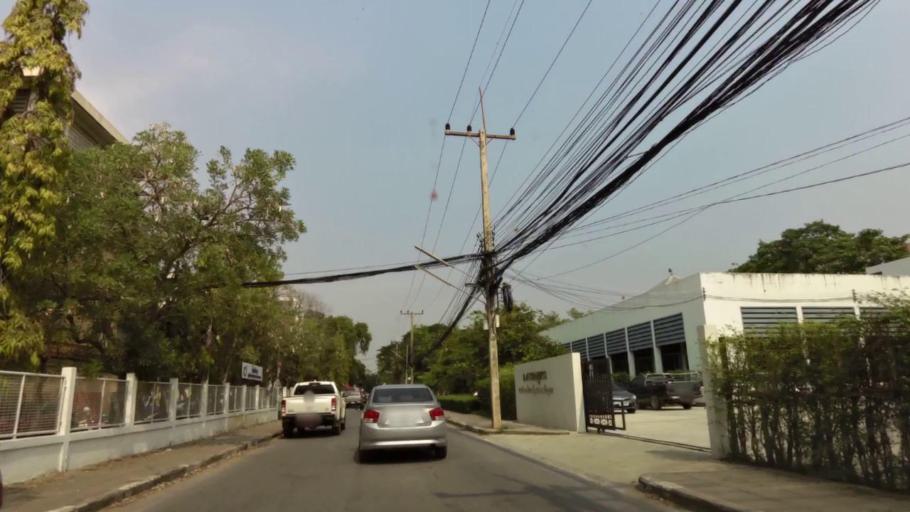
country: TH
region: Phra Nakhon Si Ayutthaya
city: Phra Nakhon Si Ayutthaya
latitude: 14.3478
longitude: 100.5652
